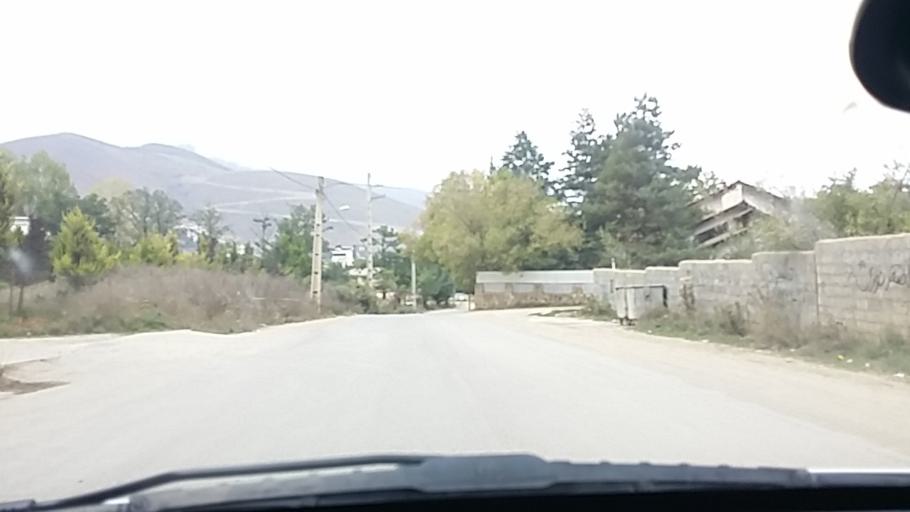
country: IR
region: Mazandaran
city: `Abbasabad
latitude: 36.4981
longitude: 51.1638
